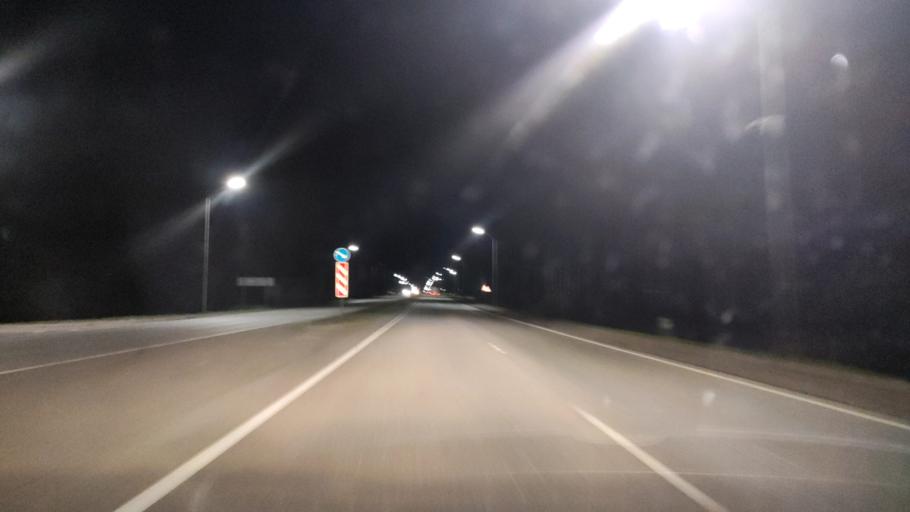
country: RU
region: Belgorod
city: Staryy Oskol
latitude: 51.3619
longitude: 37.8380
